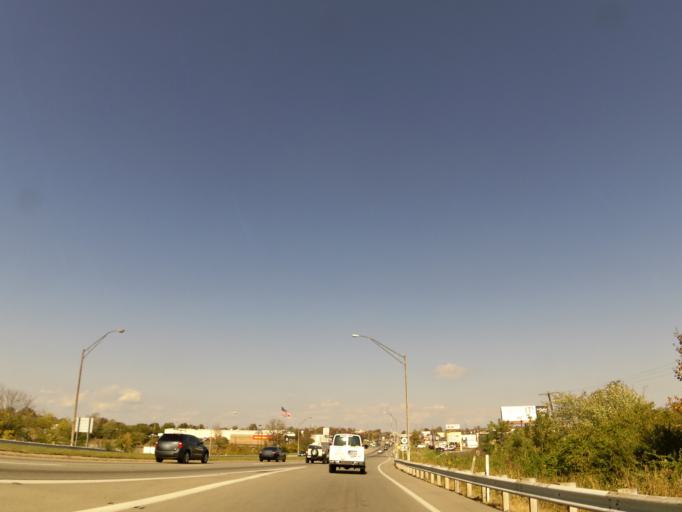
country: US
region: Kentucky
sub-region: Fayette County
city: Lexington
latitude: 38.0149
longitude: -84.4574
